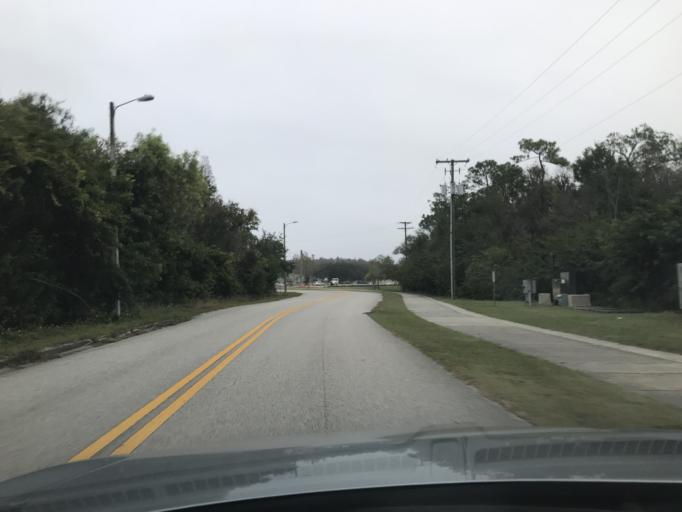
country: US
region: Florida
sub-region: Pinellas County
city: Oldsmar
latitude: 28.0490
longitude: -82.6683
